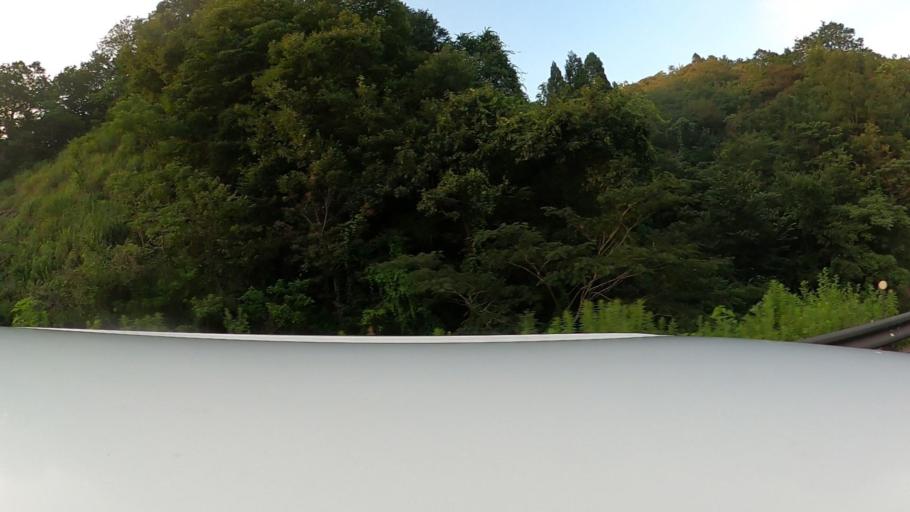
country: JP
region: Miyazaki
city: Nobeoka
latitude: 32.5773
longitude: 131.5236
